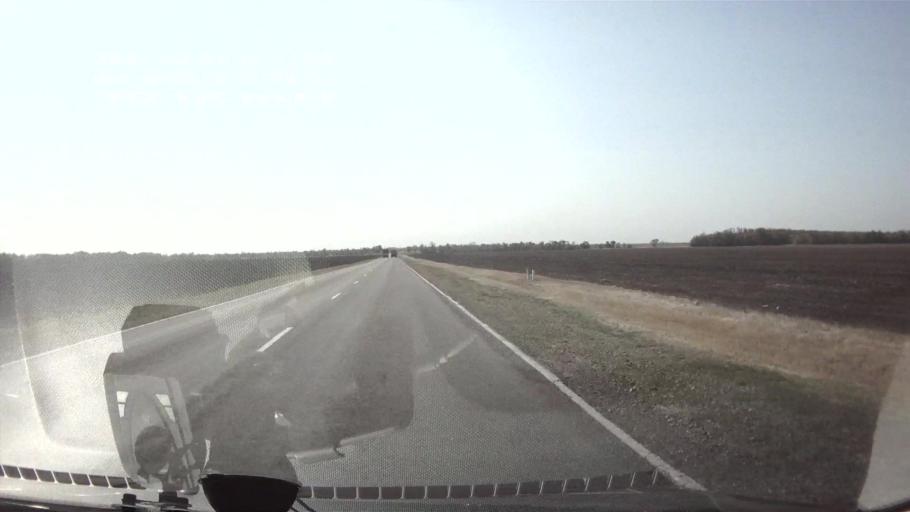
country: RU
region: Krasnodarskiy
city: Belaya Glina
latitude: 46.0274
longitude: 40.7978
